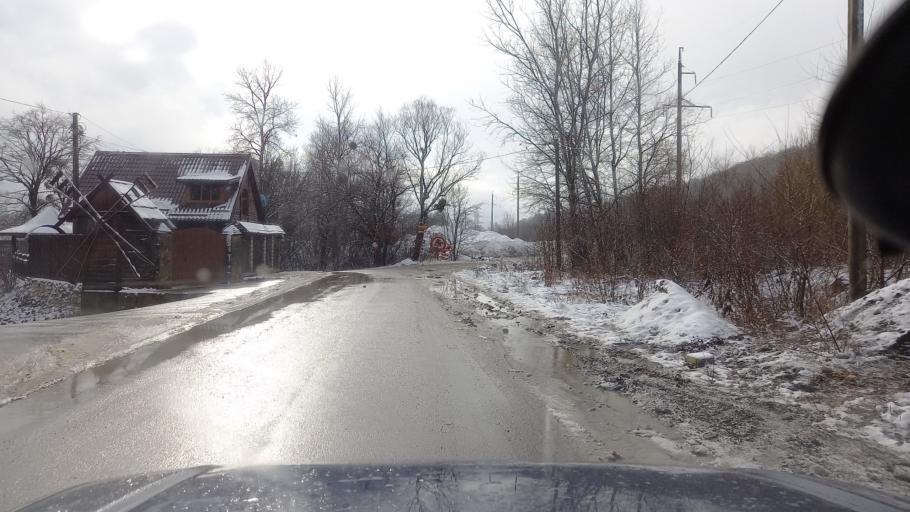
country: RU
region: Adygeya
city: Kamennomostskiy
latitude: 44.2471
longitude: 40.1986
